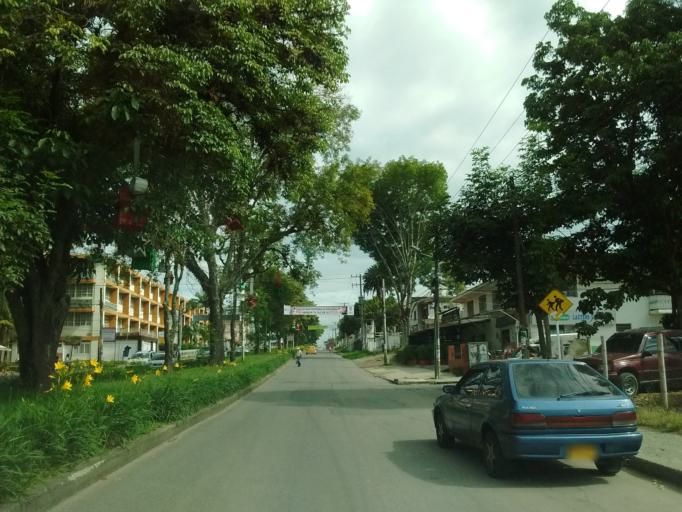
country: CO
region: Cauca
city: Popayan
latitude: 2.4487
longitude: -76.6062
